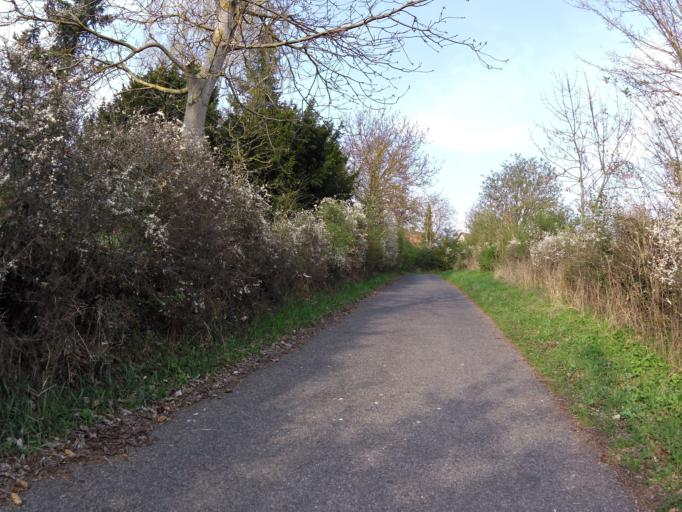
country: DE
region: Bavaria
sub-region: Regierungsbezirk Unterfranken
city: Gerbrunn
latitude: 49.7875
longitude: 10.0125
